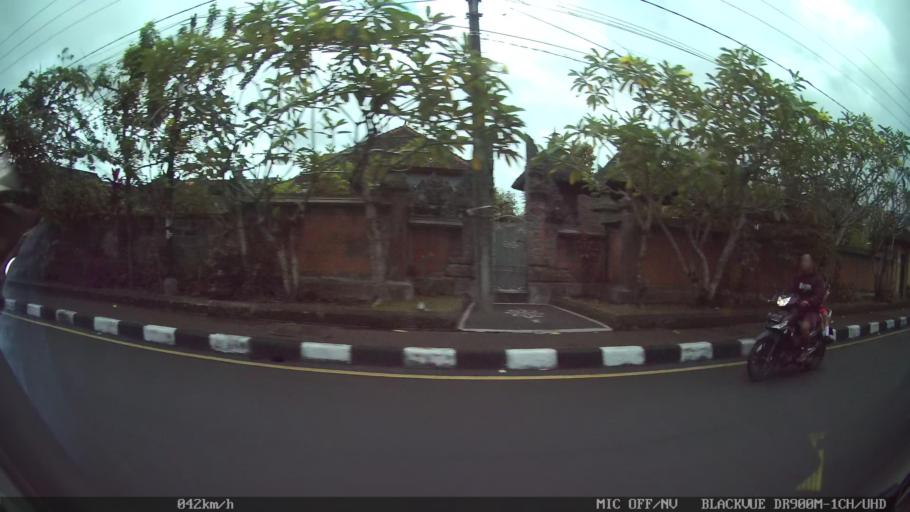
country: ID
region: Bali
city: Banjar Serangan
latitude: -8.5398
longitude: 115.1705
